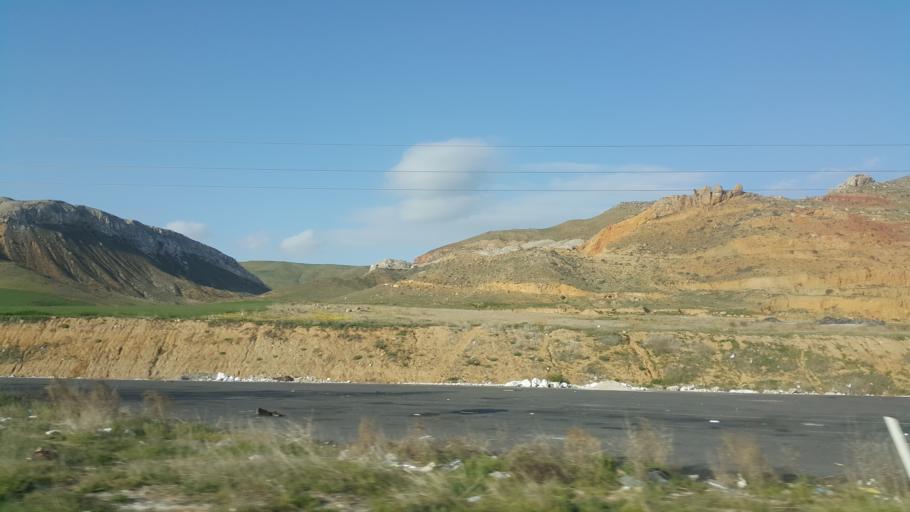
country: TR
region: Ankara
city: Sereflikochisar
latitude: 38.9881
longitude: 33.4788
